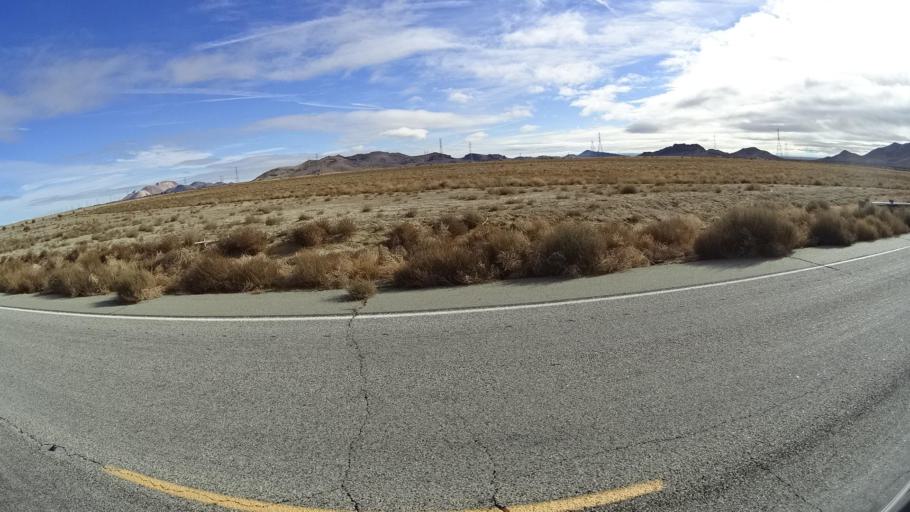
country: US
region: California
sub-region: Kern County
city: Rosamond
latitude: 34.9127
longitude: -118.2914
